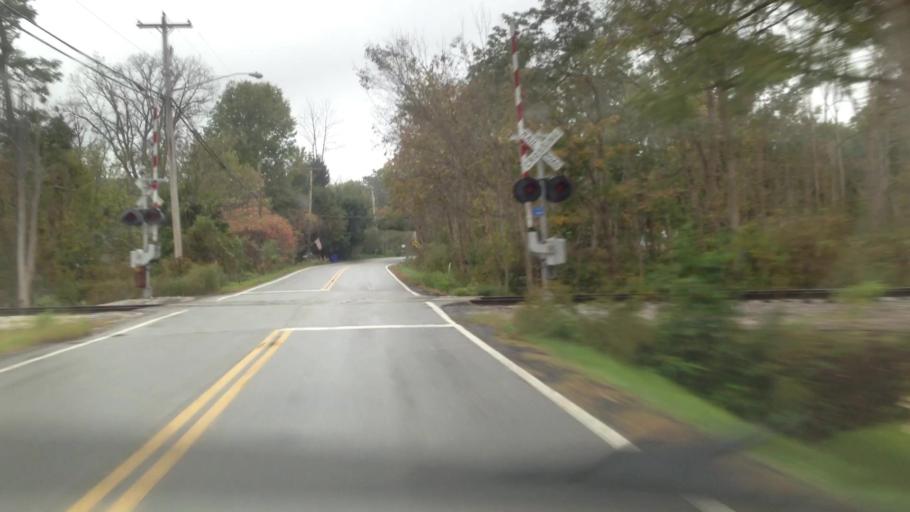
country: US
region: Ohio
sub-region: Portage County
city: Streetsboro
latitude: 41.2635
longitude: -81.3895
